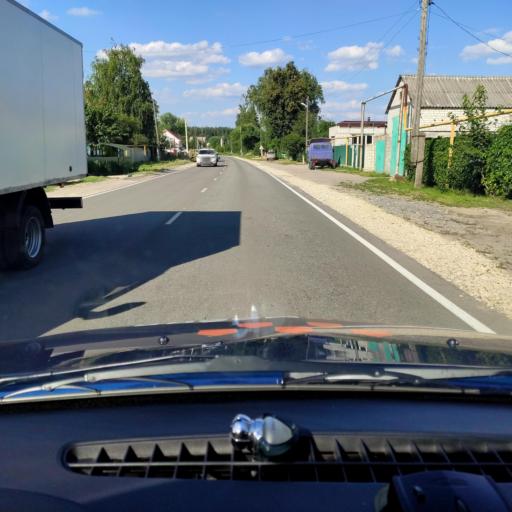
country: RU
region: Voronezj
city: Devitsa
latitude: 51.6486
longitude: 38.9706
